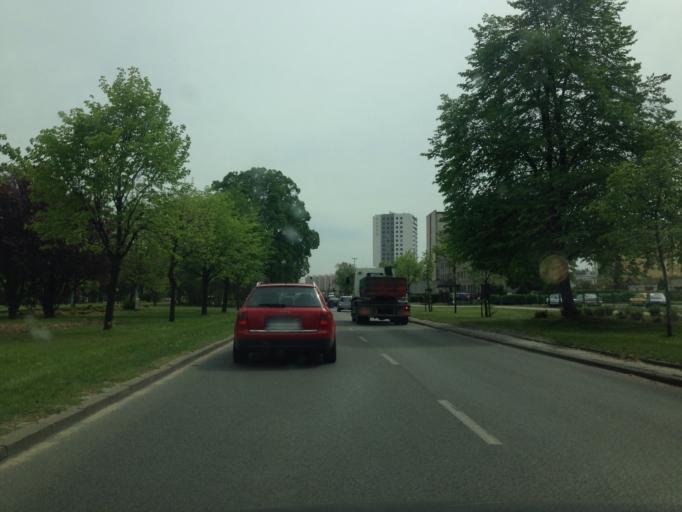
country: PL
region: Pomeranian Voivodeship
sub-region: Sopot
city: Sopot
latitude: 54.4059
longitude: 18.5898
